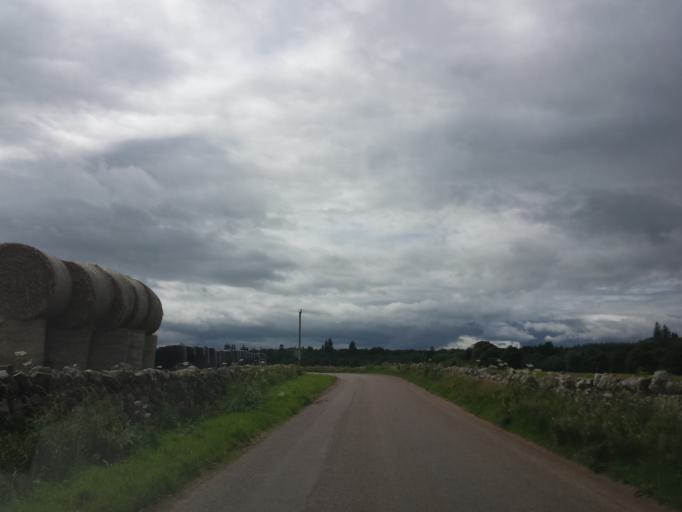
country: GB
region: Scotland
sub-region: Highland
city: Nairn
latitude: 57.5232
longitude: -3.9617
